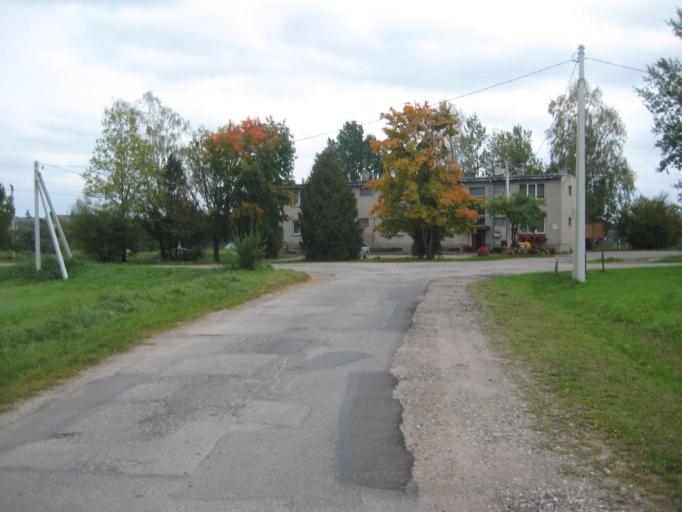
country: LT
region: Utenos apskritis
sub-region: Utena
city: Utena
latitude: 55.5261
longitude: 25.6779
